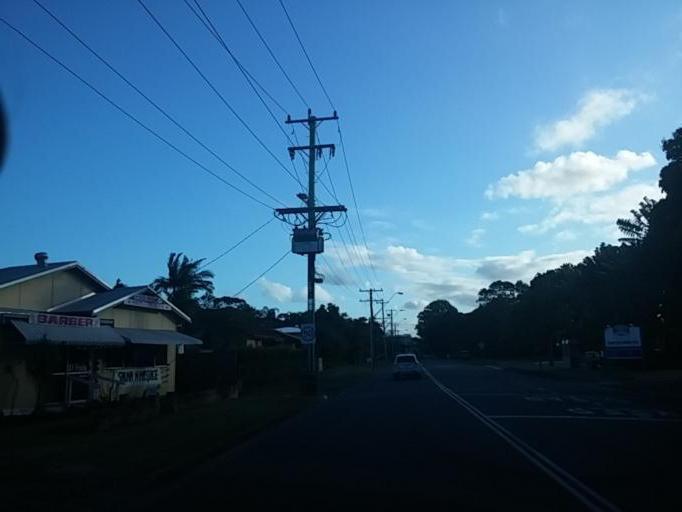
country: AU
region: New South Wales
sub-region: Tweed
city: Tweed Heads West
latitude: -28.1877
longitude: 153.5398
